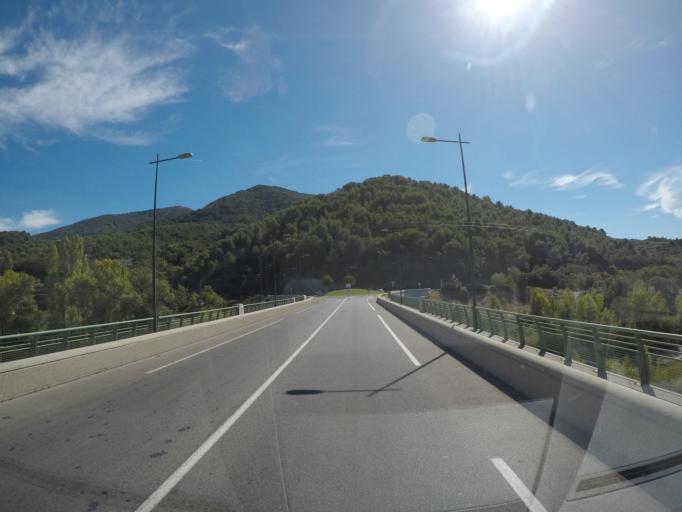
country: FR
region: Rhone-Alpes
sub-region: Departement de la Drome
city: Nyons
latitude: 44.3478
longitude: 5.1198
